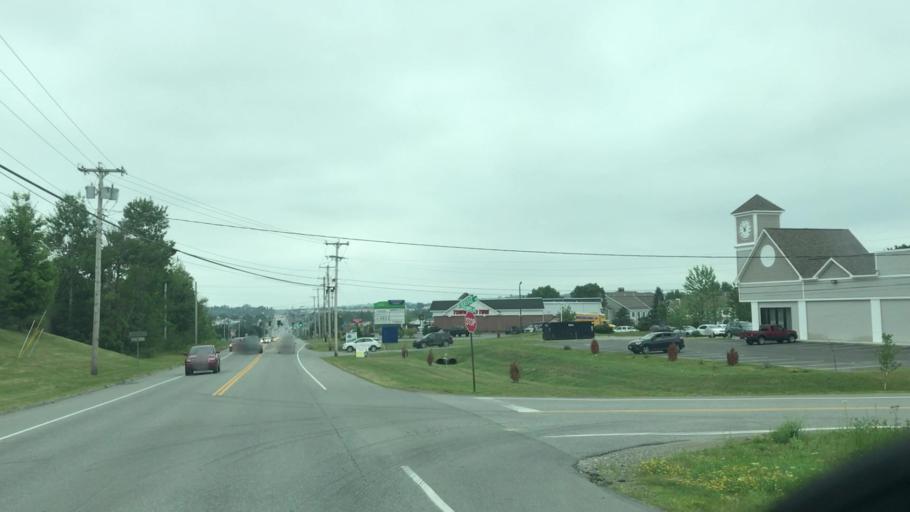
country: US
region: Maine
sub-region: Penobscot County
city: Veazie
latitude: 44.8426
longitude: -68.7430
